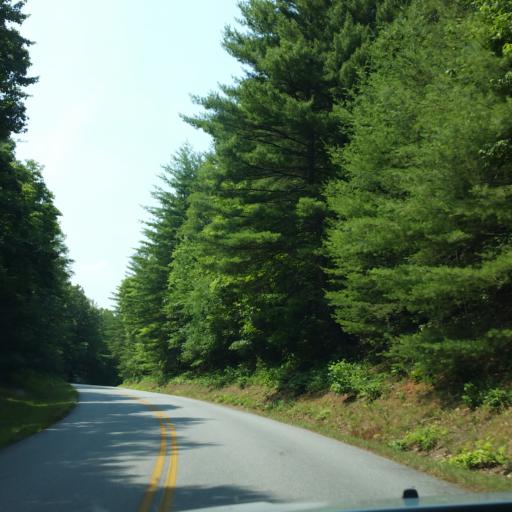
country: US
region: North Carolina
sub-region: Buncombe County
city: Biltmore Forest
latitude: 35.5113
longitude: -82.5569
